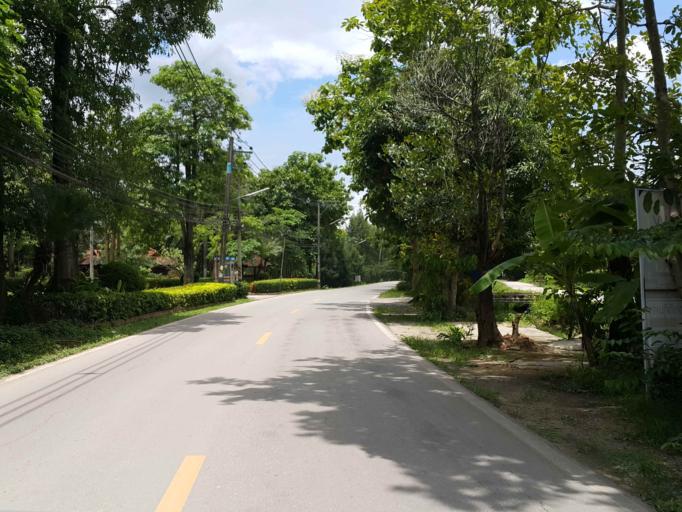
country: TH
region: Chiang Mai
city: San Sai
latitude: 18.8538
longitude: 98.9863
